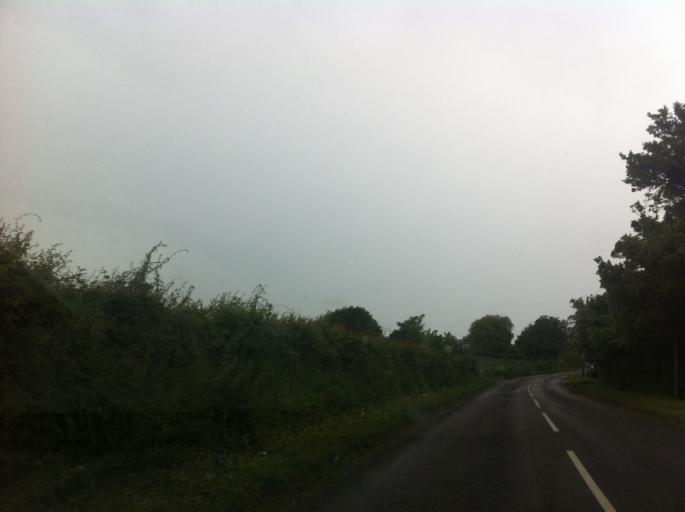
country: GB
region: England
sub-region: Northamptonshire
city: Earls Barton
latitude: 52.2636
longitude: -0.7152
